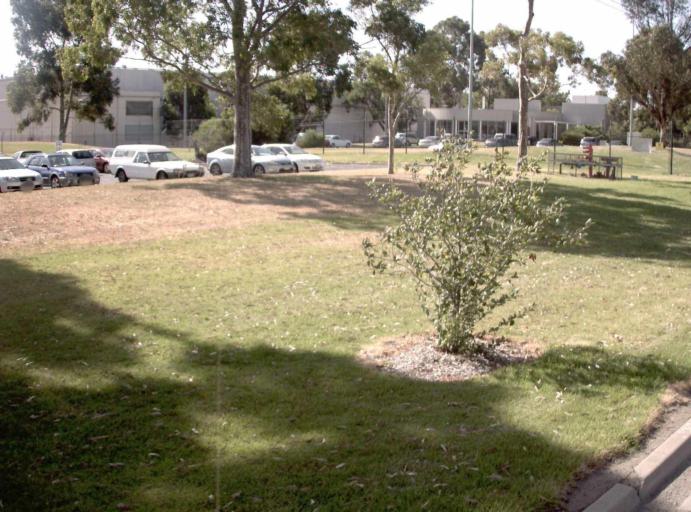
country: AU
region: Victoria
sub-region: Casey
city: Hampton Park
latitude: -38.0313
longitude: 145.2119
